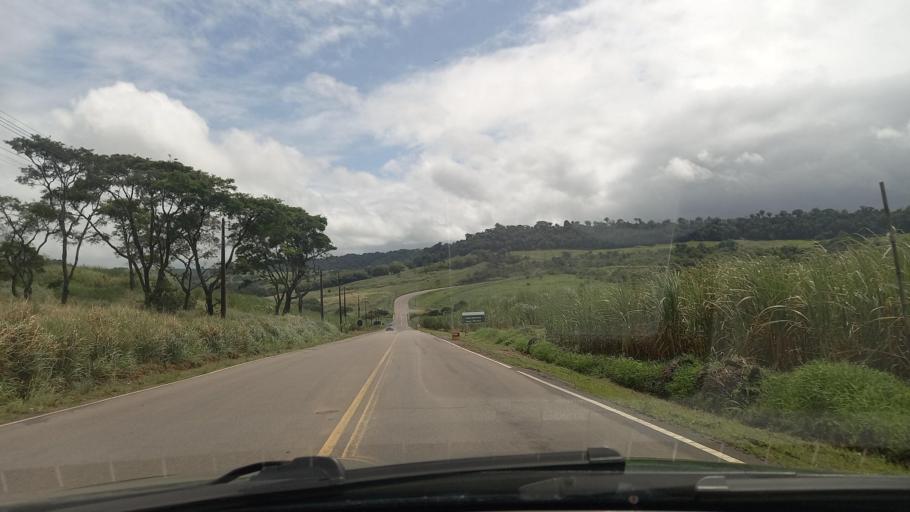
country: BR
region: Alagoas
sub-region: Sao Miguel Dos Campos
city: Sao Miguel dos Campos
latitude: -9.8177
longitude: -36.2194
